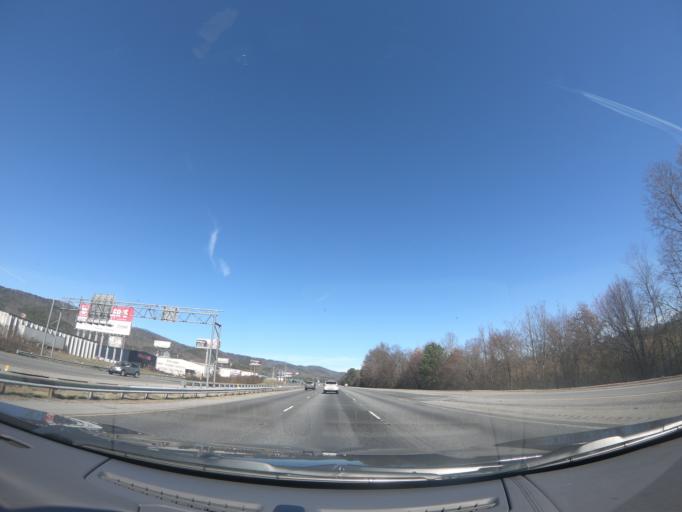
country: US
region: Georgia
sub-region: Whitfield County
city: Dalton
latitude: 34.6898
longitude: -85.0024
